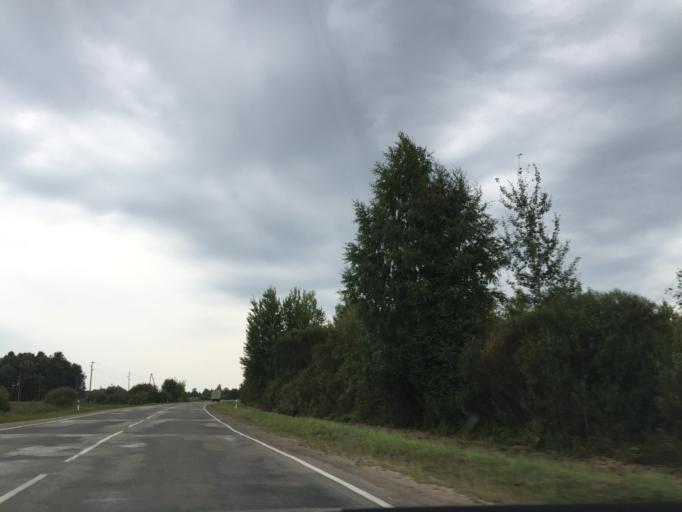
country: LV
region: Ludzas Rajons
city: Ludza
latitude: 56.5276
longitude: 27.7133
